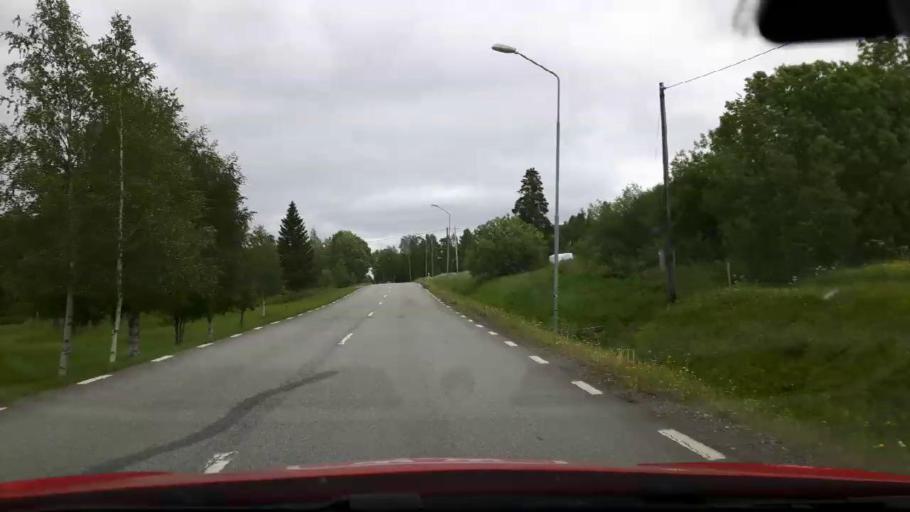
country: SE
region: Jaemtland
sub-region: Stroemsunds Kommun
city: Stroemsund
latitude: 63.5743
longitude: 15.3777
